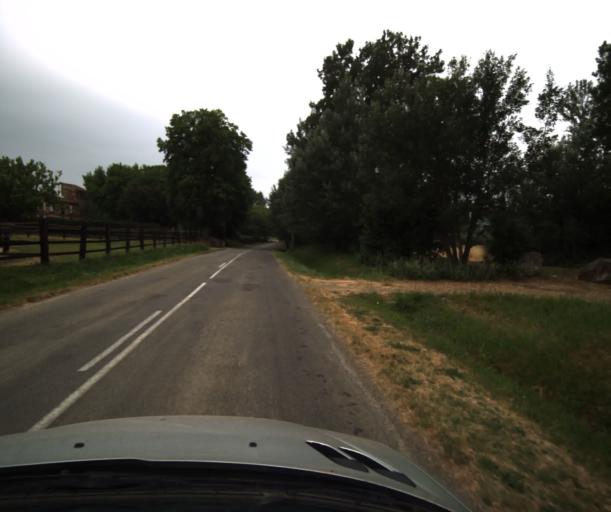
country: FR
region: Midi-Pyrenees
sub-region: Departement du Tarn-et-Garonne
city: Saint-Nicolas-de-la-Grave
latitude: 44.0827
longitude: 1.0259
